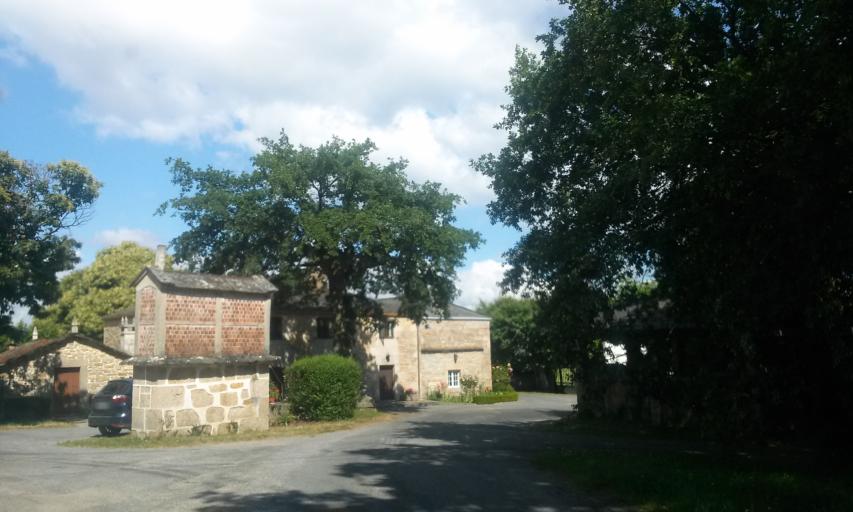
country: ES
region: Galicia
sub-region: Provincia de Lugo
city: Begonte
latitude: 43.1189
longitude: -7.6726
